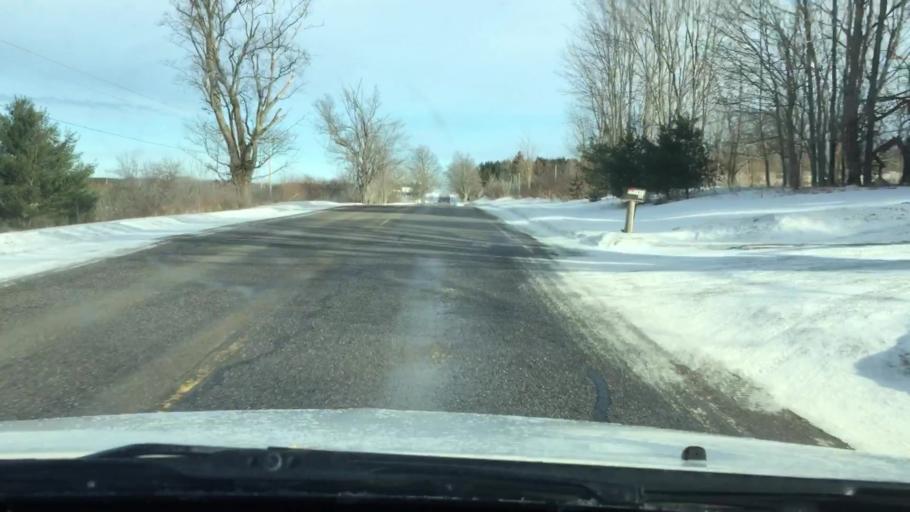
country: US
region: Michigan
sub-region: Kalkaska County
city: Kalkaska
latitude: 44.6407
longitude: -85.2218
